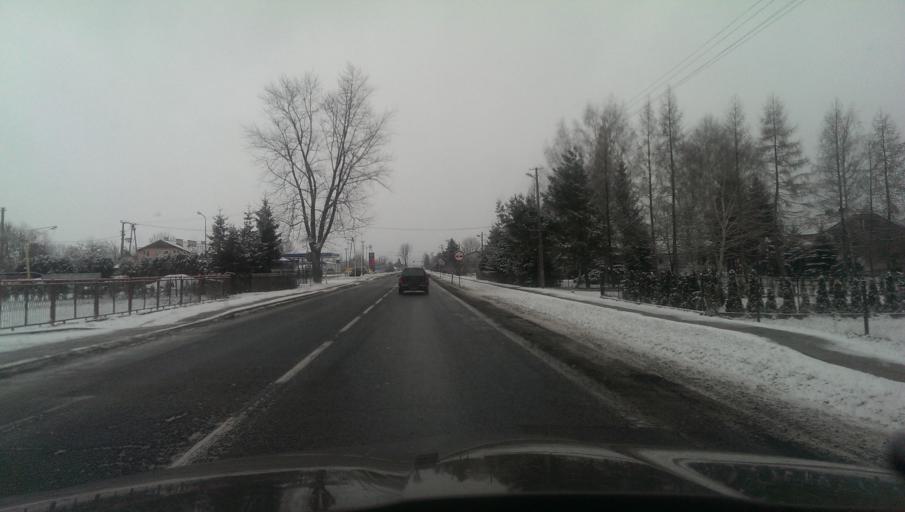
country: PL
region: Subcarpathian Voivodeship
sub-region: Powiat sanocki
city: Besko
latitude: 49.5858
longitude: 21.9599
